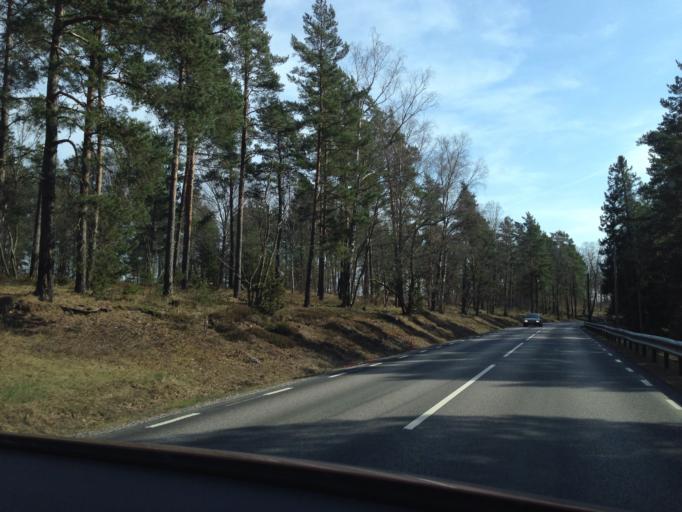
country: SE
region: Stockholm
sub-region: Botkyrka Kommun
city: Eriksberg
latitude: 59.2309
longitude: 17.7833
